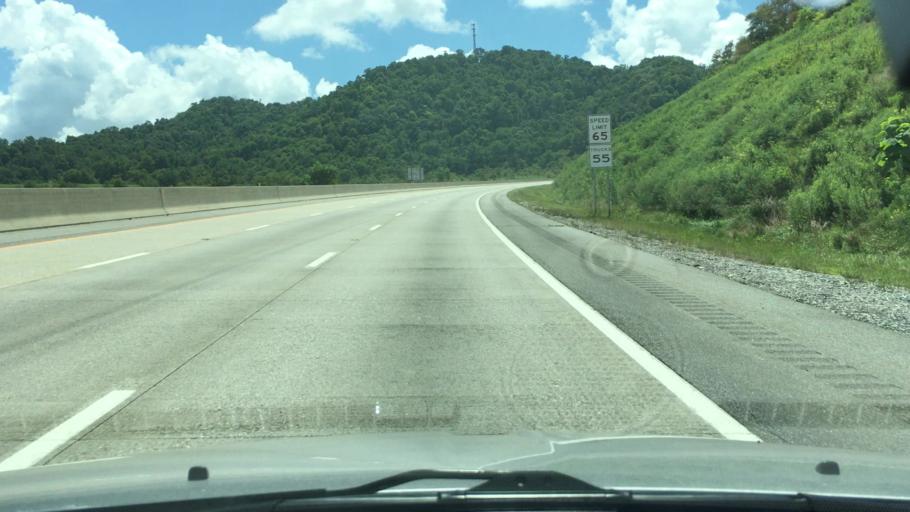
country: US
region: North Carolina
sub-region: Madison County
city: Mars Hill
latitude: 35.9027
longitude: -82.5486
